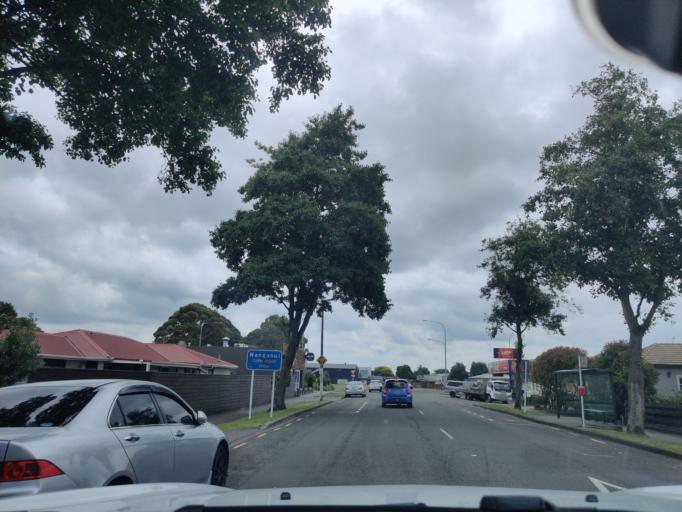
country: NZ
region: Manawatu-Wanganui
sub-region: Palmerston North City
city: Palmerston North
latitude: -40.3517
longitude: 175.5854
